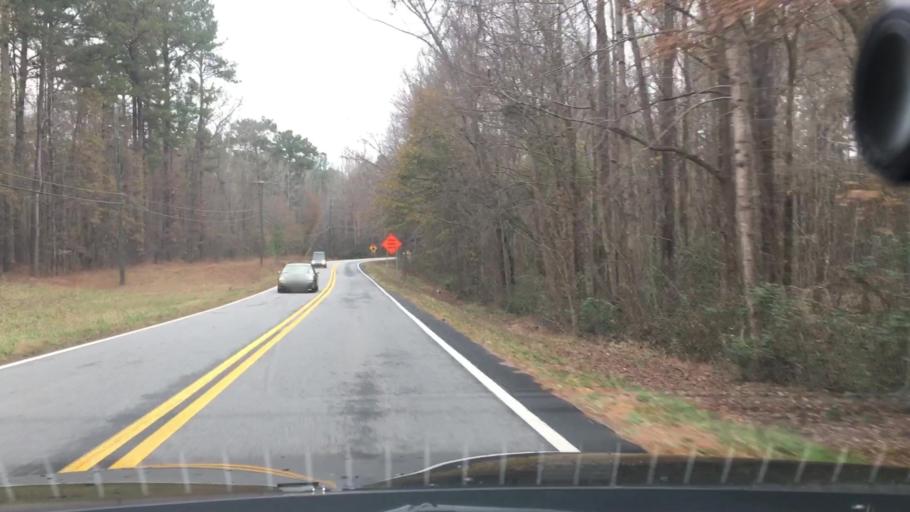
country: US
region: Georgia
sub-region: Coweta County
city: East Newnan
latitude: 33.4195
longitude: -84.7026
